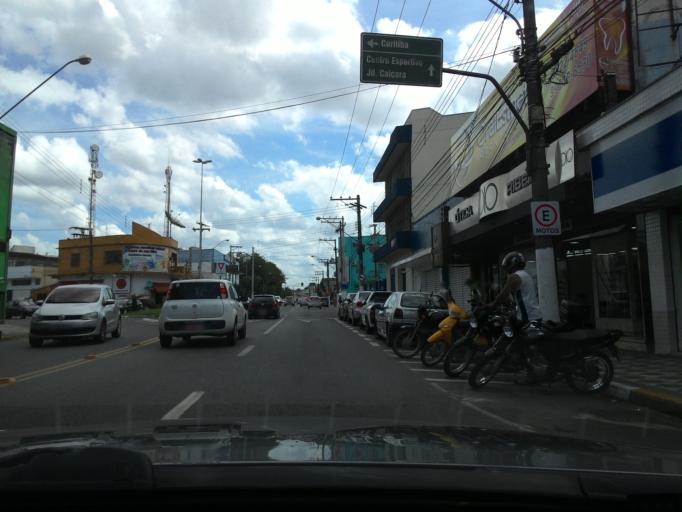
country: BR
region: Sao Paulo
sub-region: Registro
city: Registro
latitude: -24.4960
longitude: -47.8470
